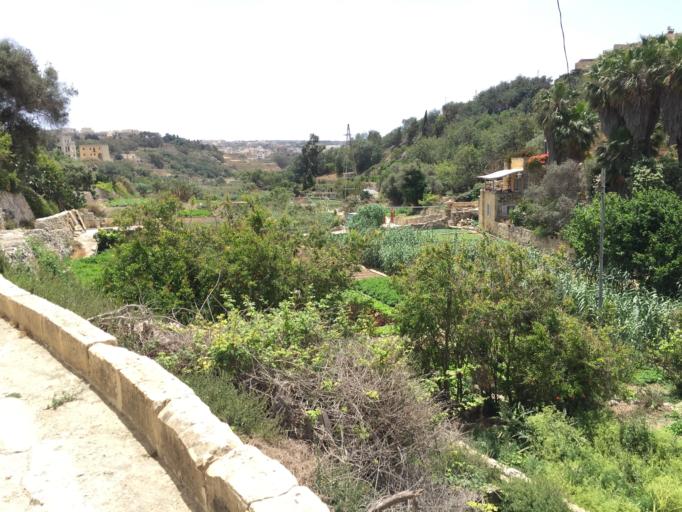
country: MT
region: Il-Fontana
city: Fontana
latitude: 36.0407
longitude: 14.2330
